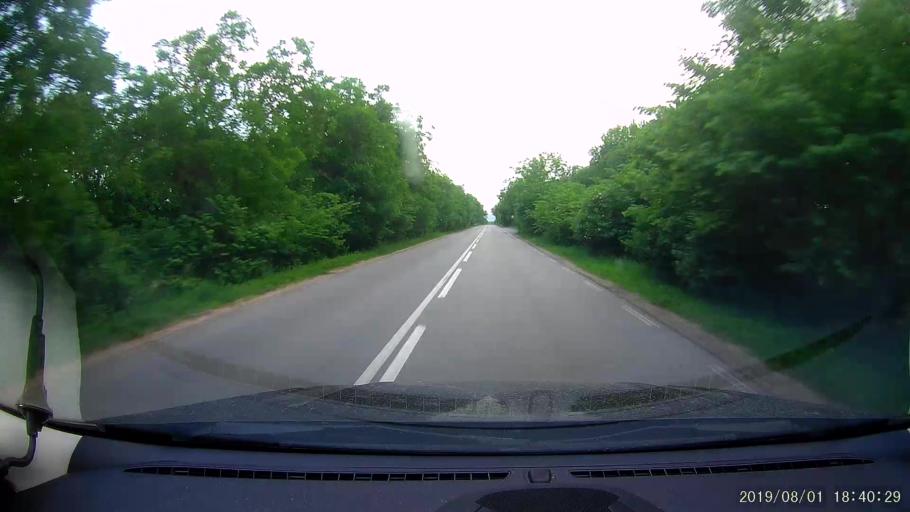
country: BG
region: Shumen
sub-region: Obshtina Khitrino
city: Gara Khitrino
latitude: 43.3660
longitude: 26.9194
